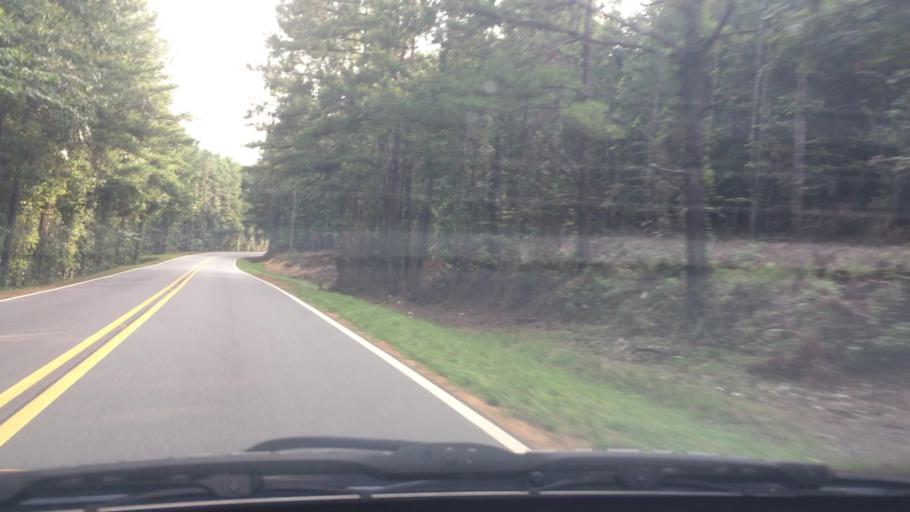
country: US
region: Alabama
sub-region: Shelby County
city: Helena
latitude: 33.2513
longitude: -86.9477
